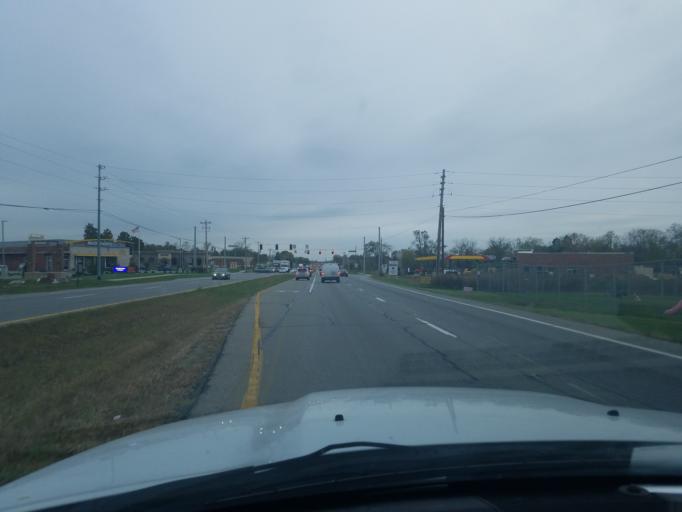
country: US
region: Indiana
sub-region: Clark County
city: Oak Park
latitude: 38.3588
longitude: -85.7014
